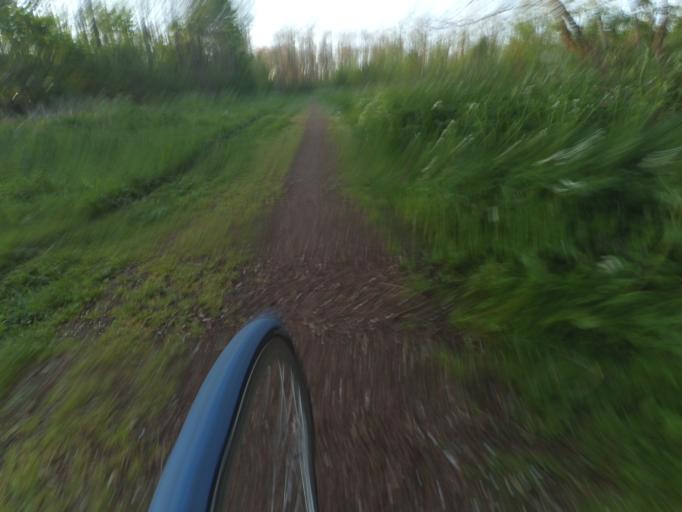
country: NL
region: Flevoland
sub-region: Gemeente Lelystad
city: Lelystad
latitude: 52.4322
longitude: 5.4962
